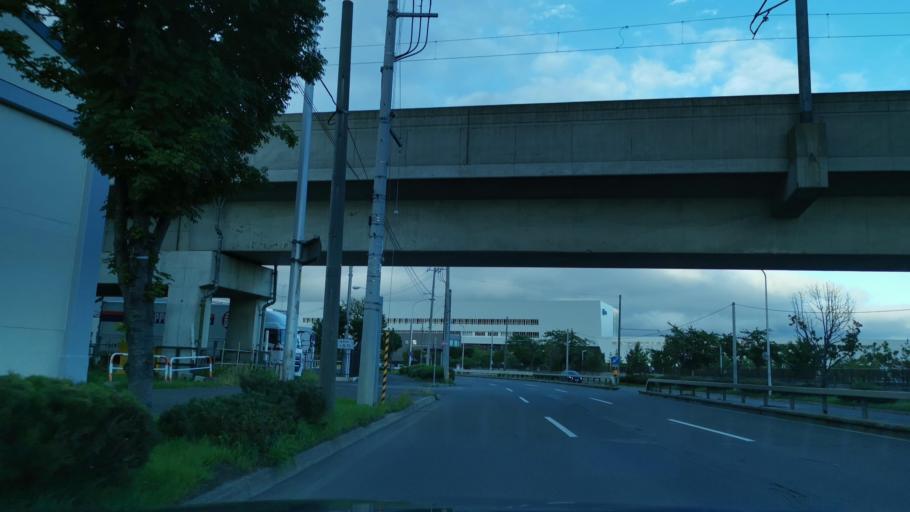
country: JP
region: Hokkaido
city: Sapporo
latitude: 43.0767
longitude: 141.3205
